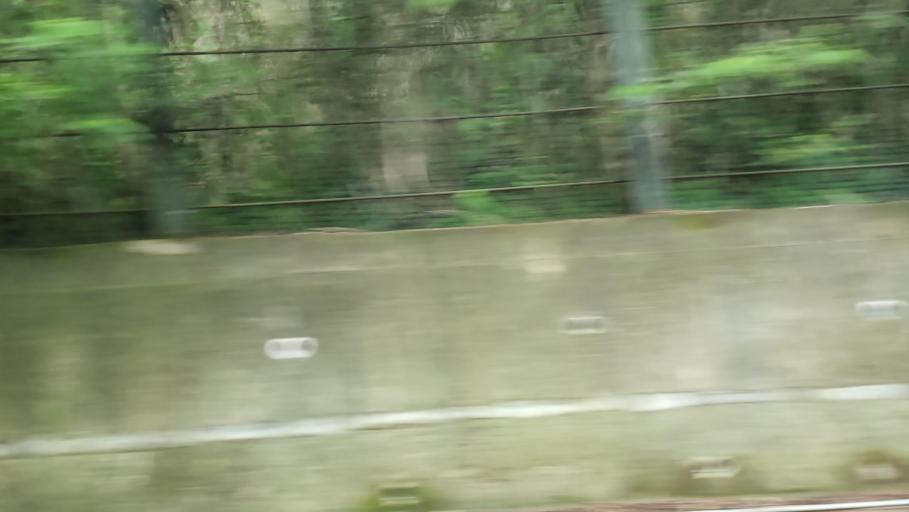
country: TW
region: Taipei
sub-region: Taipei
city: Banqiao
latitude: 24.8928
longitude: 121.4284
